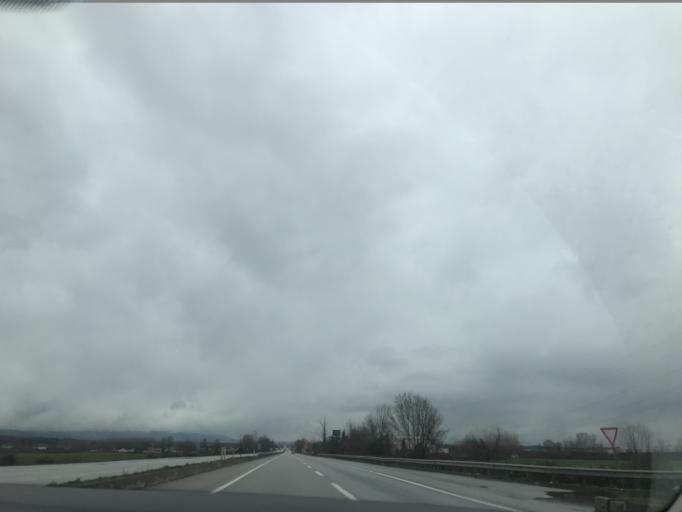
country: TR
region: Sakarya
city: Akyazi
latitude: 40.7708
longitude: 30.6302
